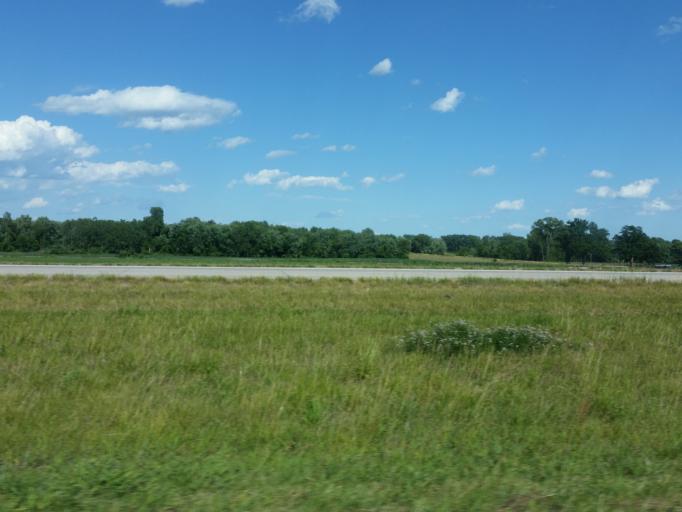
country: US
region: Missouri
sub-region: Lewis County
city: Canton
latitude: 40.2073
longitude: -91.5247
